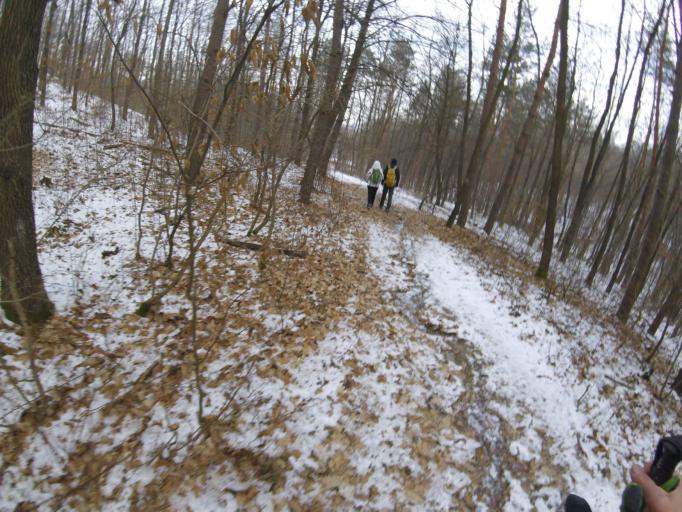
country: HU
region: Heves
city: Sirok
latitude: 47.9092
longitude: 20.1689
